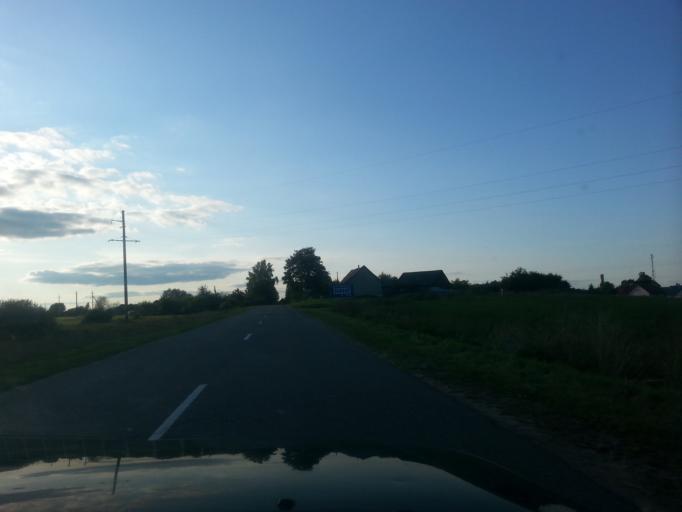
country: BY
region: Minsk
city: Narach
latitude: 55.0558
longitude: 26.6140
